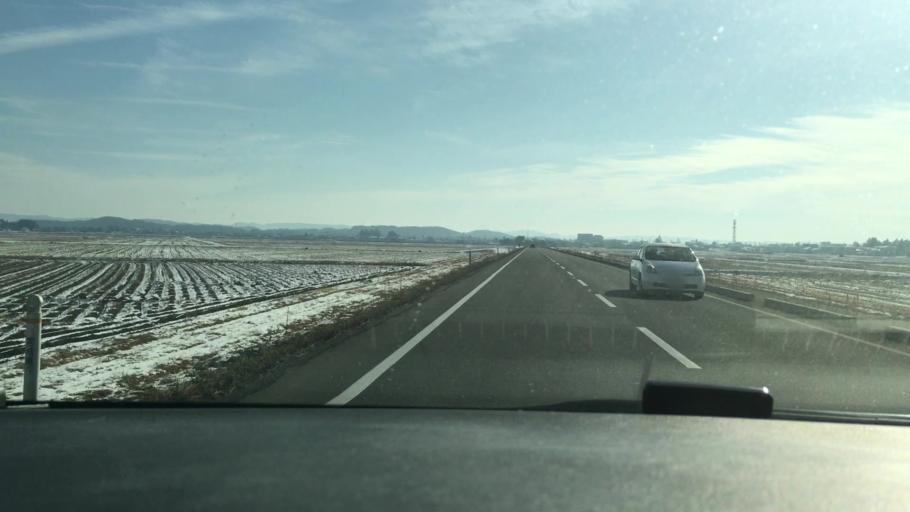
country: JP
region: Iwate
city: Ichinoseki
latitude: 38.7828
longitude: 141.1222
